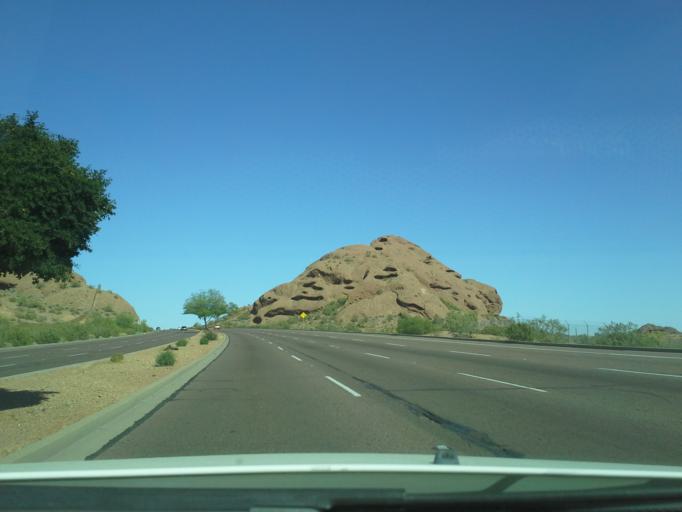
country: US
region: Arizona
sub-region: Maricopa County
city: Tempe Junction
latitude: 33.4655
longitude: -111.9588
